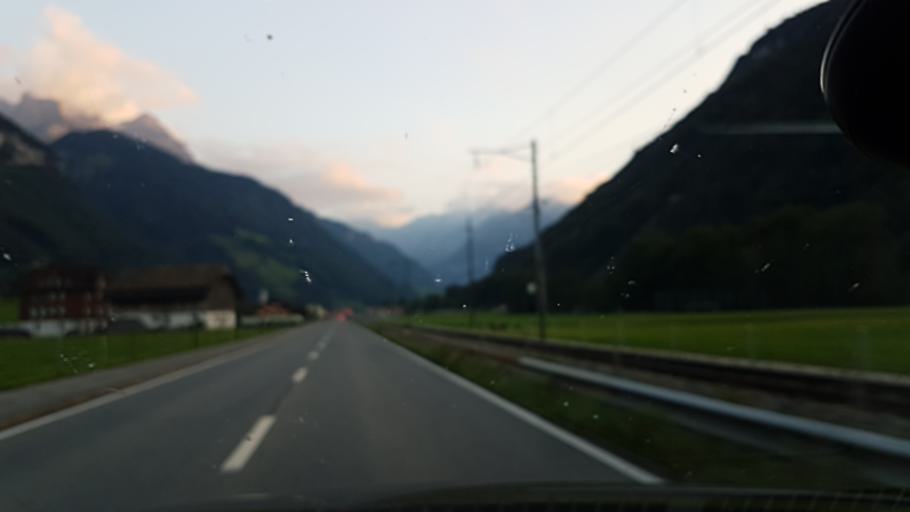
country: CH
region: Nidwalden
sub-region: Nidwalden
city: Dallenwil
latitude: 46.9174
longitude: 8.3966
